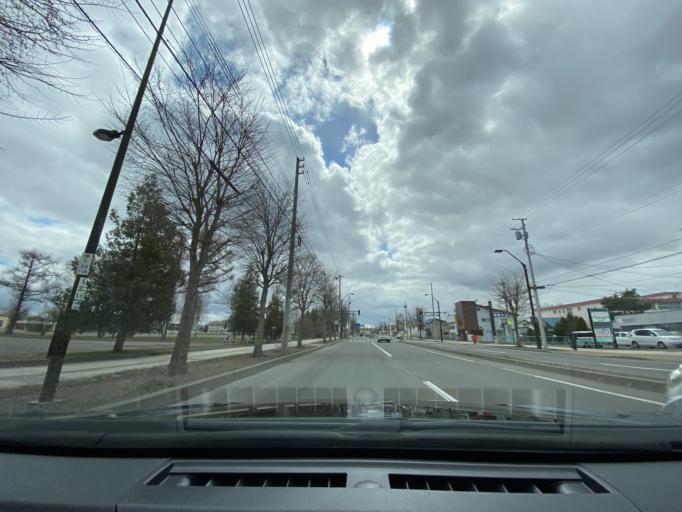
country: JP
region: Hokkaido
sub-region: Asahikawa-shi
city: Asahikawa
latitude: 43.7573
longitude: 142.3498
